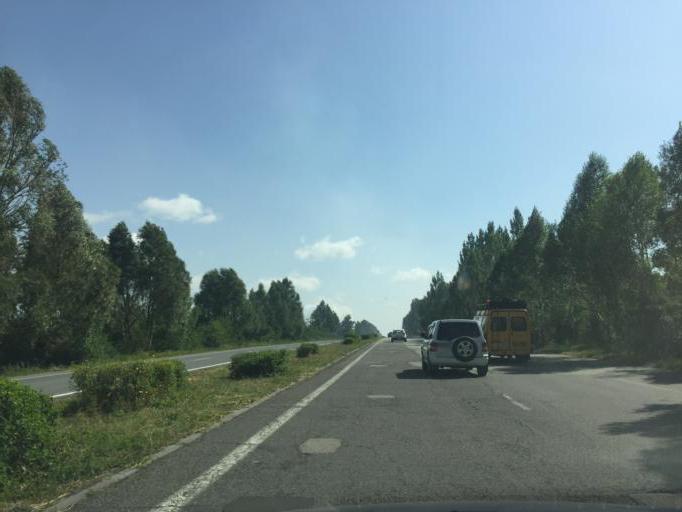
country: AM
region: Kotayk'i Marz
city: Hrazdan
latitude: 40.4745
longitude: 44.7498
